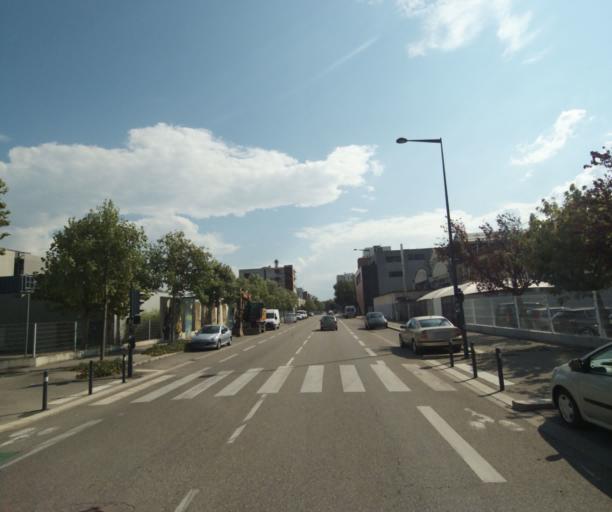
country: FR
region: Rhone-Alpes
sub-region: Departement de l'Isere
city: Seyssinet-Pariset
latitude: 45.1741
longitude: 5.7051
